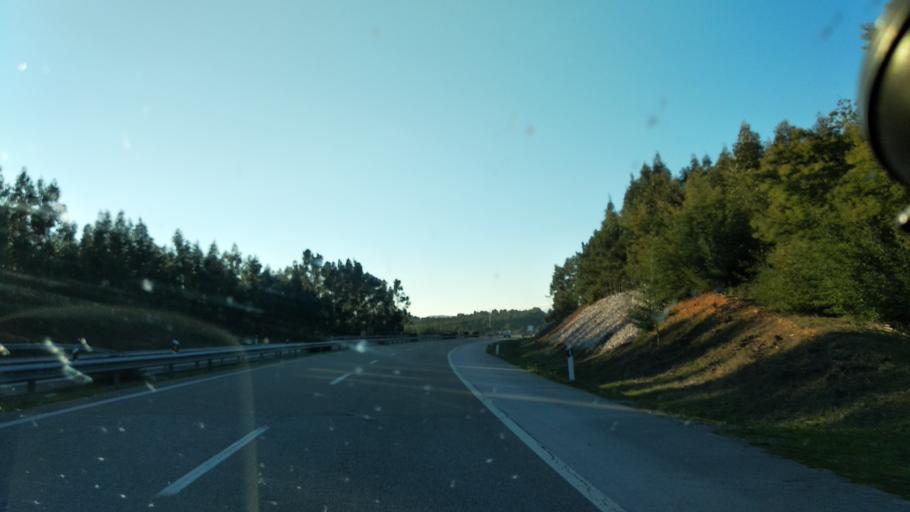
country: PT
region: Santarem
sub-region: Constancia
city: Constancia
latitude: 39.4845
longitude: -8.3710
